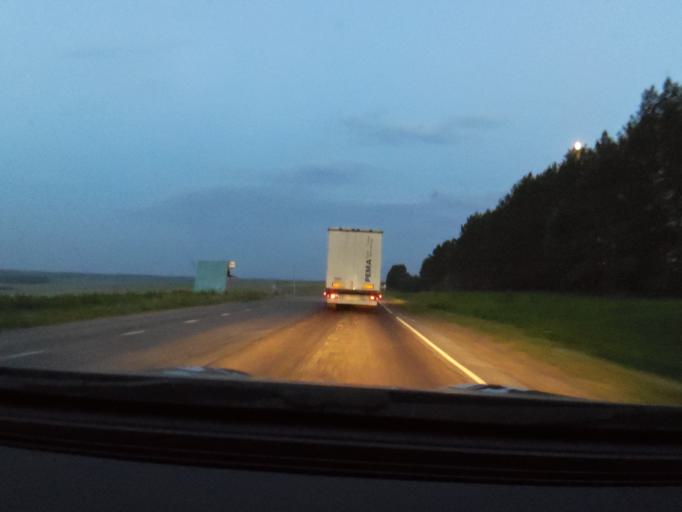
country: RU
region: Bashkortostan
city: Duvan
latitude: 56.0506
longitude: 58.1985
